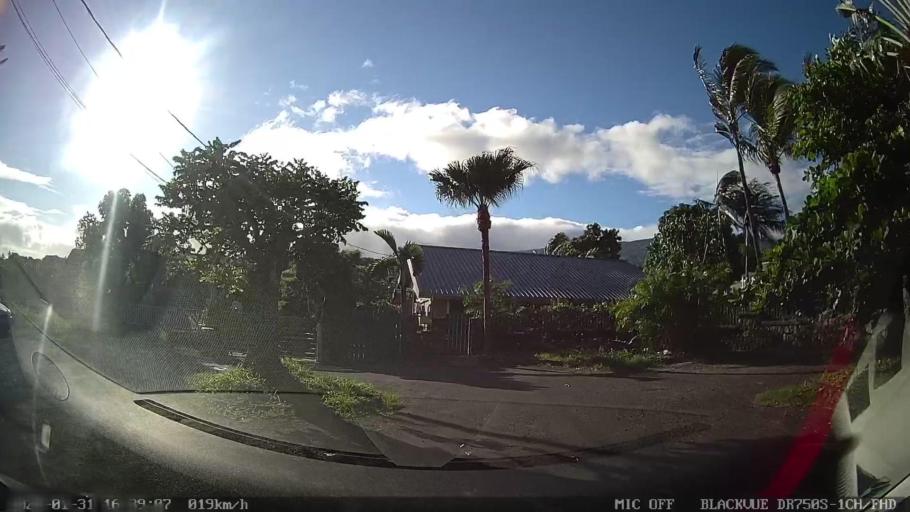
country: RE
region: Reunion
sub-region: Reunion
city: Saint-Denis
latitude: -20.9094
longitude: 55.4890
